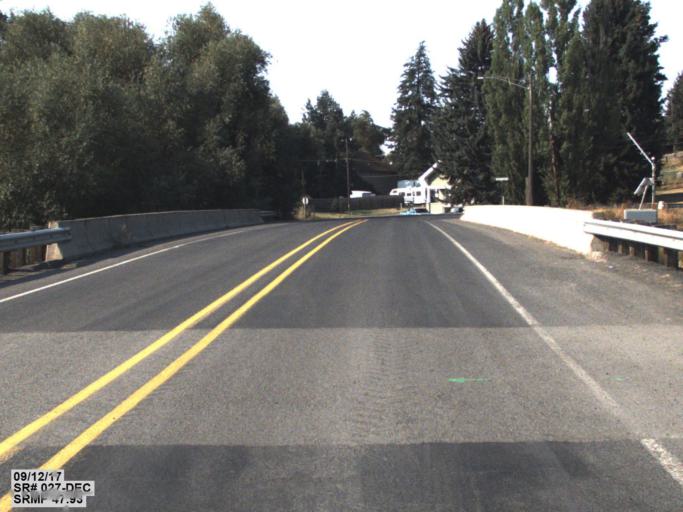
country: US
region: Idaho
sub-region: Benewah County
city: Plummer
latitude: 47.2202
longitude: -117.0746
